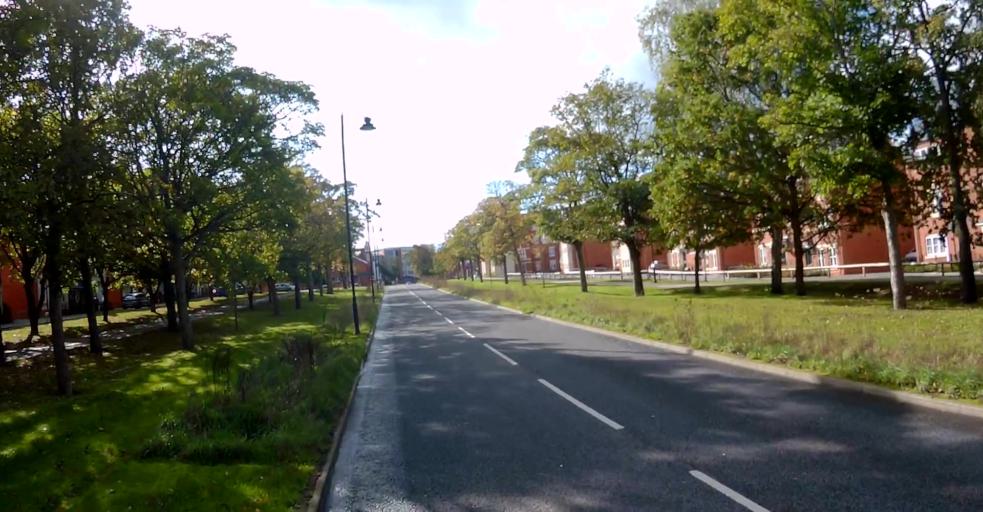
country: GB
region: England
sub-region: Hampshire
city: Aldershot
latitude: 51.2566
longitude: -0.7635
